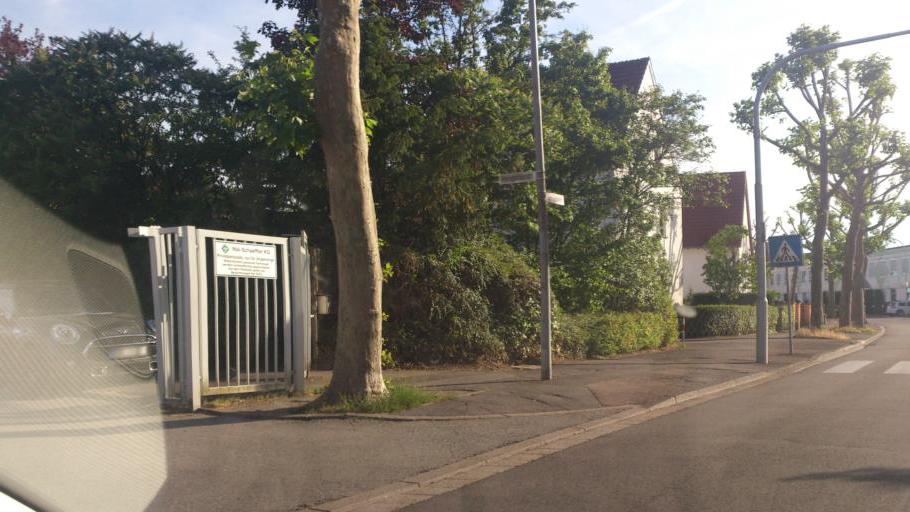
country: DE
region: Saarland
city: Homburg
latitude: 49.3313
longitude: 7.3327
